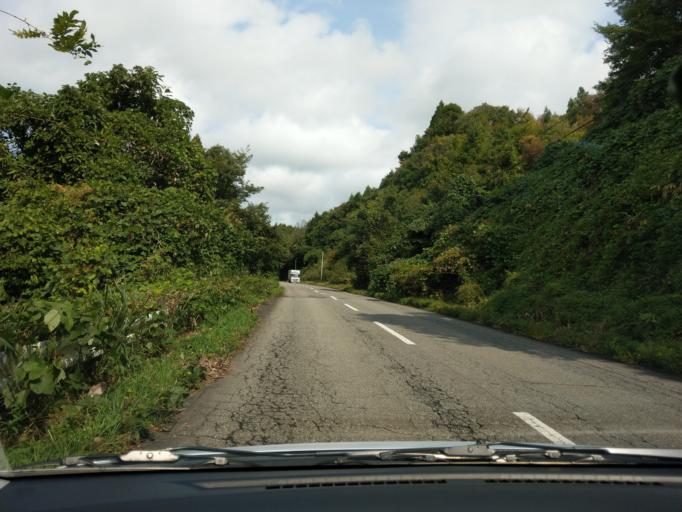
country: JP
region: Akita
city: Omagari
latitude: 39.4862
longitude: 140.3131
